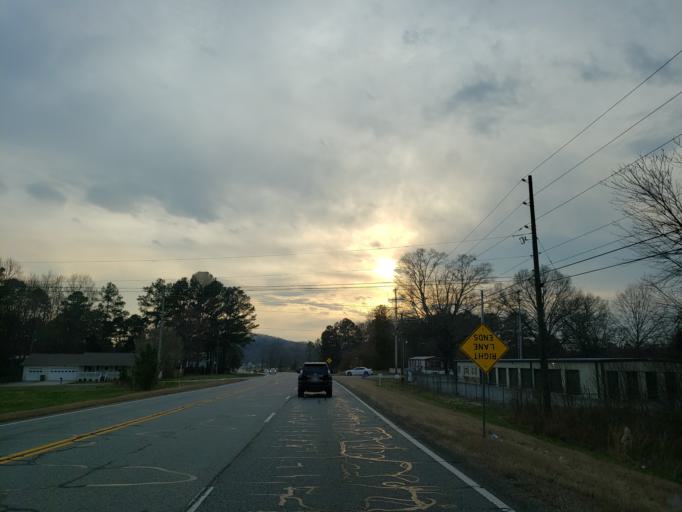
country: US
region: Georgia
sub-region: Whitfield County
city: Varnell
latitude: 34.8752
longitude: -85.0048
